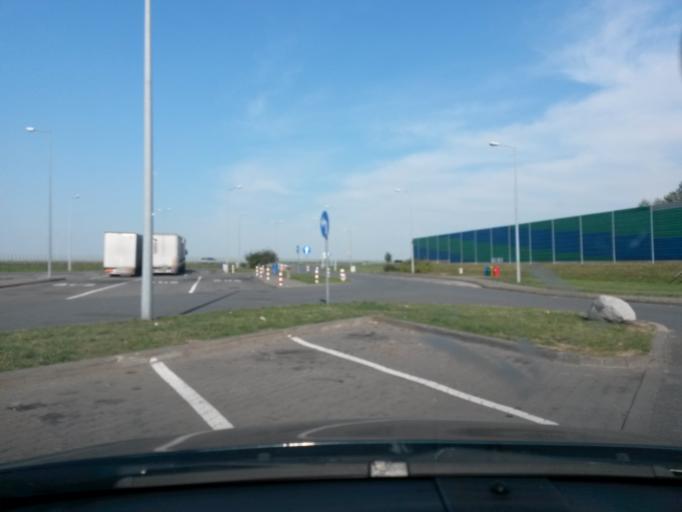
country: PL
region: Greater Poland Voivodeship
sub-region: Powiat wrzesinski
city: Kolaczkowo
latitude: 52.2934
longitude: 17.6530
